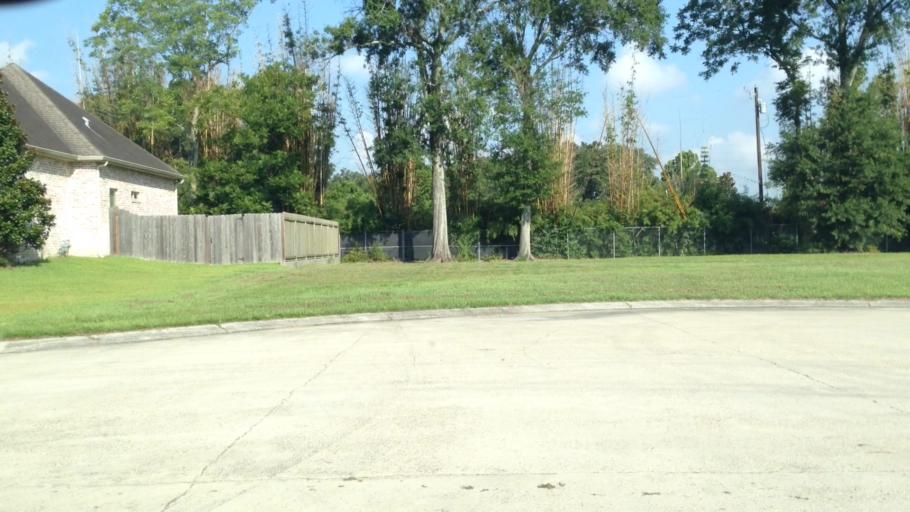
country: US
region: Louisiana
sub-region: Jefferson Parish
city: Jefferson
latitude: 29.9481
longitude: -90.1559
